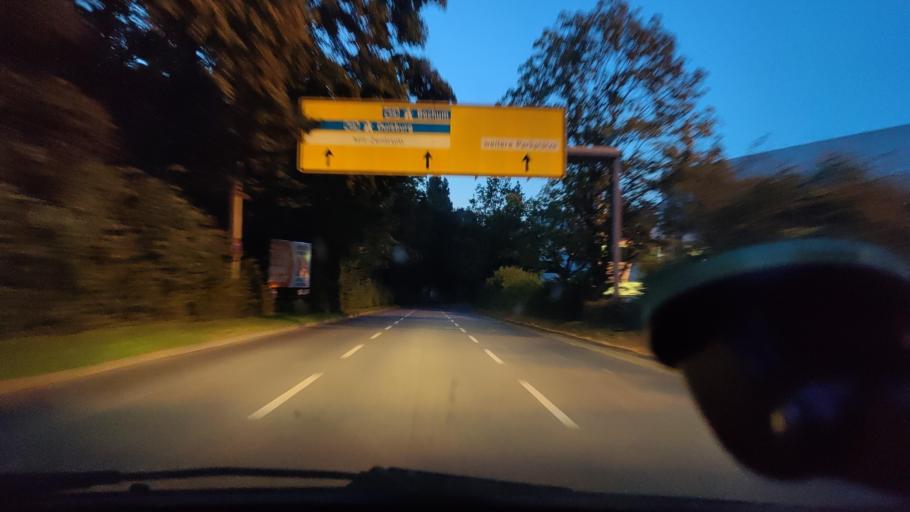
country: DE
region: North Rhine-Westphalia
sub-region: Regierungsbezirk Dusseldorf
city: Essen
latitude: 51.4381
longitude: 6.9517
